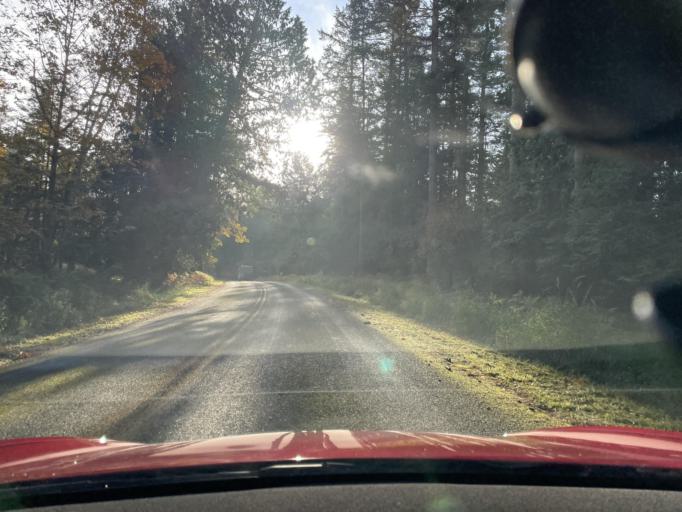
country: US
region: Washington
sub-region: San Juan County
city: Friday Harbor
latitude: 48.5305
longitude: -123.1560
